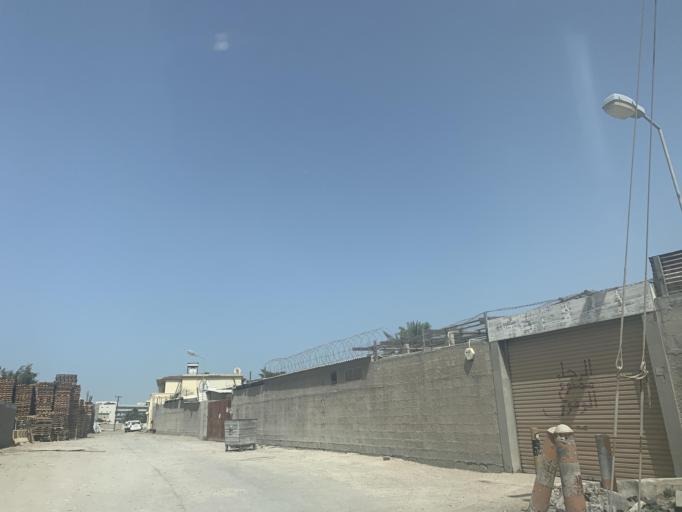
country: BH
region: Northern
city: Sitrah
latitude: 26.1732
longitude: 50.6138
